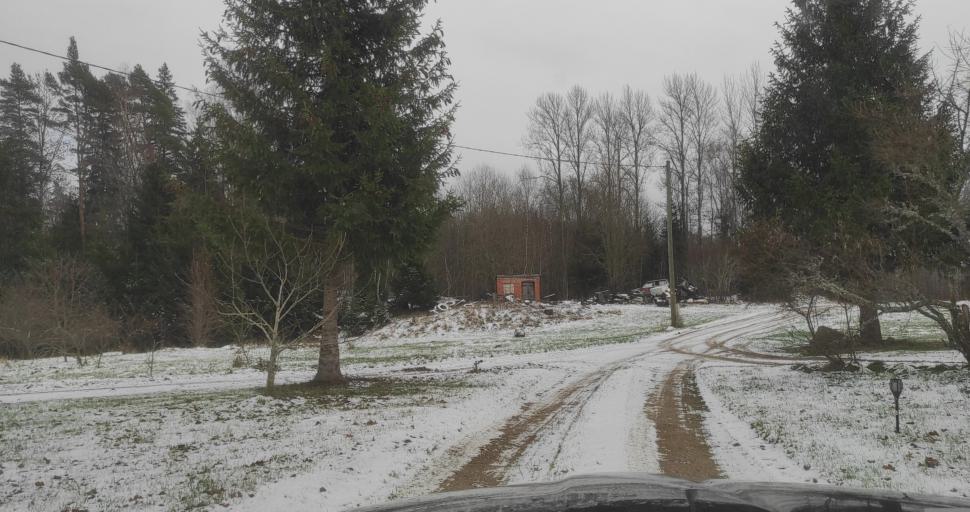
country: LV
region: Alsunga
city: Alsunga
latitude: 56.9601
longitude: 21.6415
